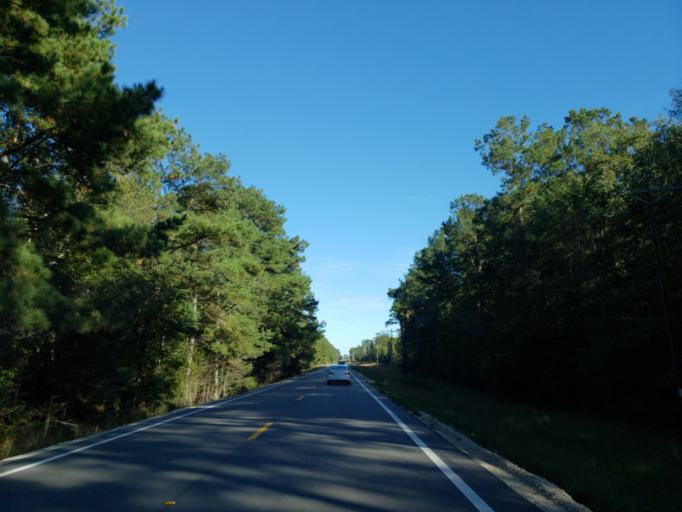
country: US
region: Mississippi
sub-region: Perry County
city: Richton
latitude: 31.3650
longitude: -89.0553
